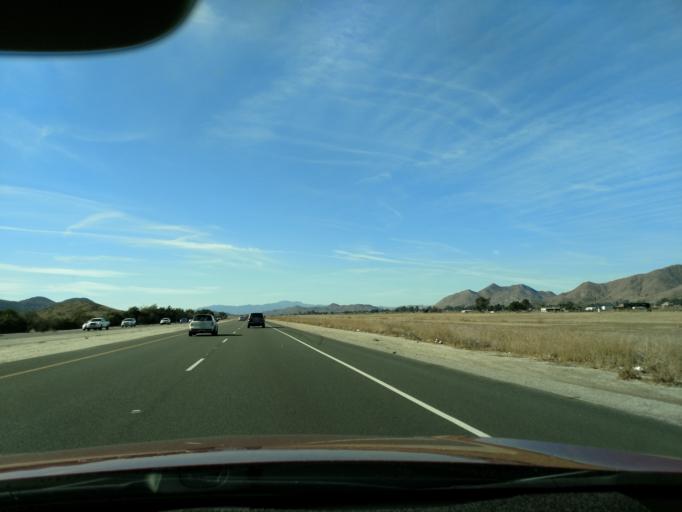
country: US
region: California
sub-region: Riverside County
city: Winchester
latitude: 33.6985
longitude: -117.0534
